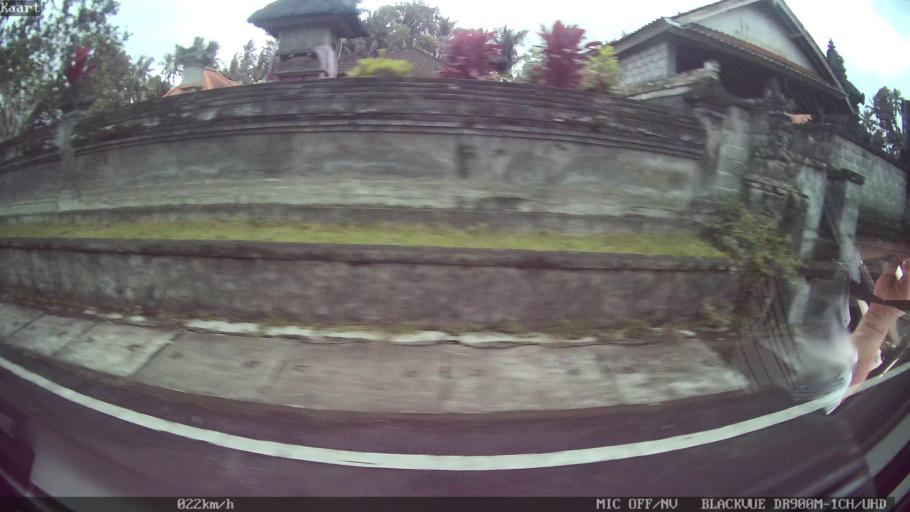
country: ID
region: Bali
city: Pemijian
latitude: -8.4478
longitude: 115.2281
